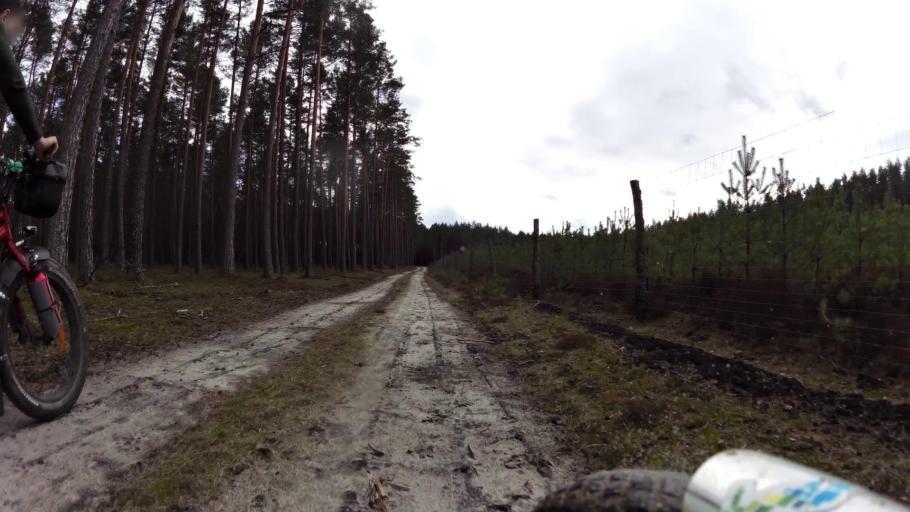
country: PL
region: Pomeranian Voivodeship
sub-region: Powiat bytowski
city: Kolczyglowy
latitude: 54.1601
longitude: 17.1894
